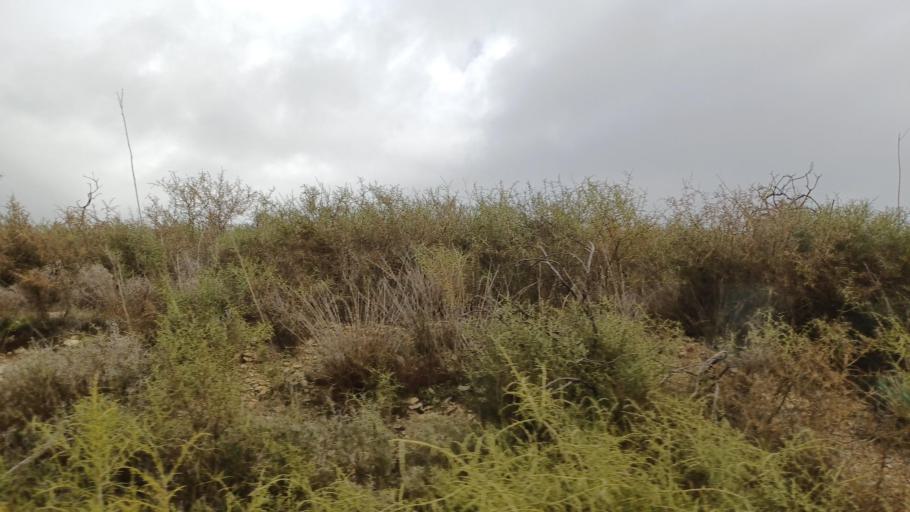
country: CY
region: Limassol
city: Pachna
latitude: 34.8253
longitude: 32.7382
